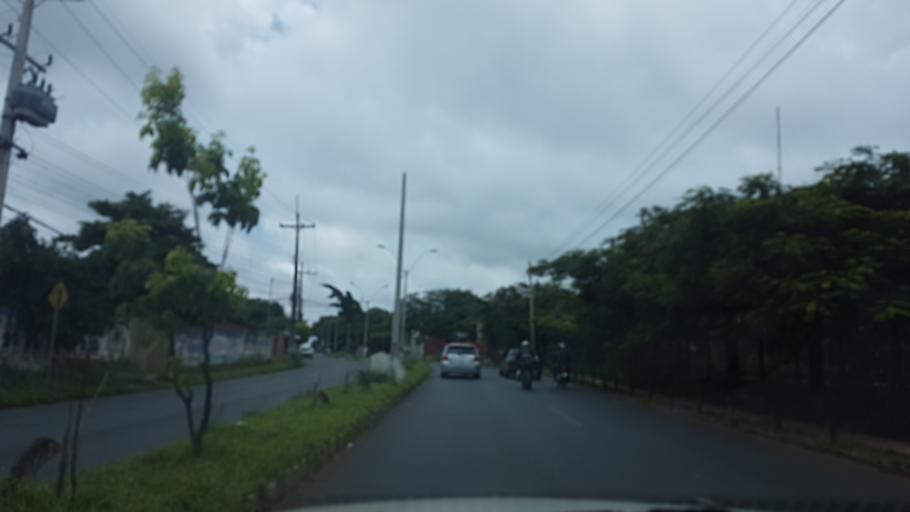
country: PY
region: Central
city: Villa Elisa
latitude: -25.3879
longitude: -57.5829
